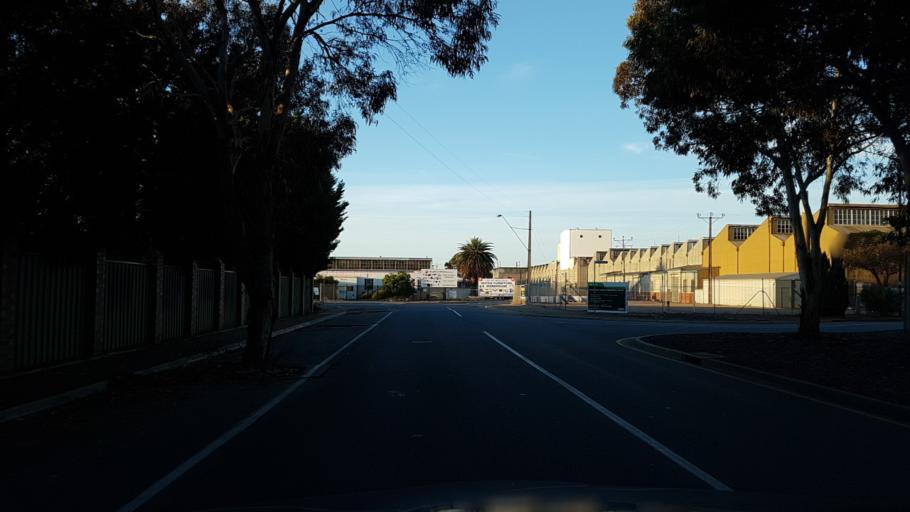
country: AU
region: South Australia
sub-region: Charles Sturt
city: Woodville North
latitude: -34.8661
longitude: 138.5382
